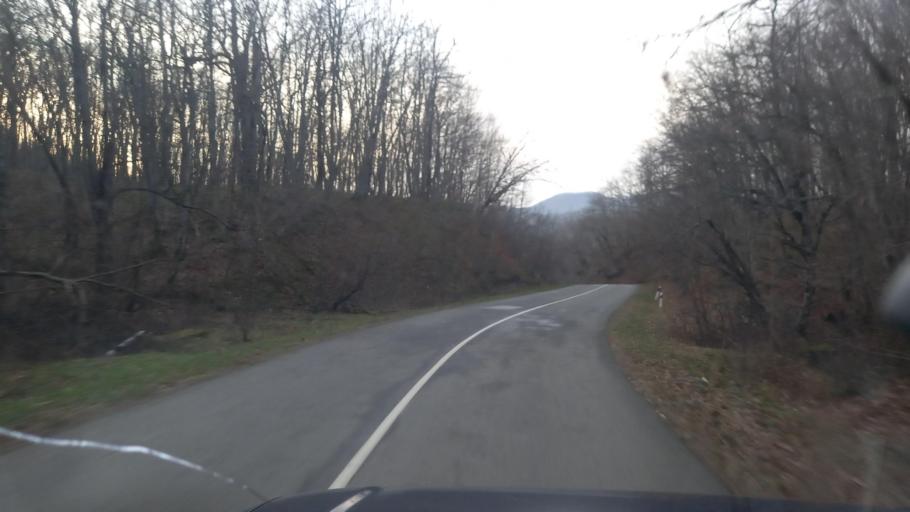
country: RU
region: Krasnodarskiy
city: Goryachiy Klyuch
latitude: 44.3877
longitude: 39.1799
